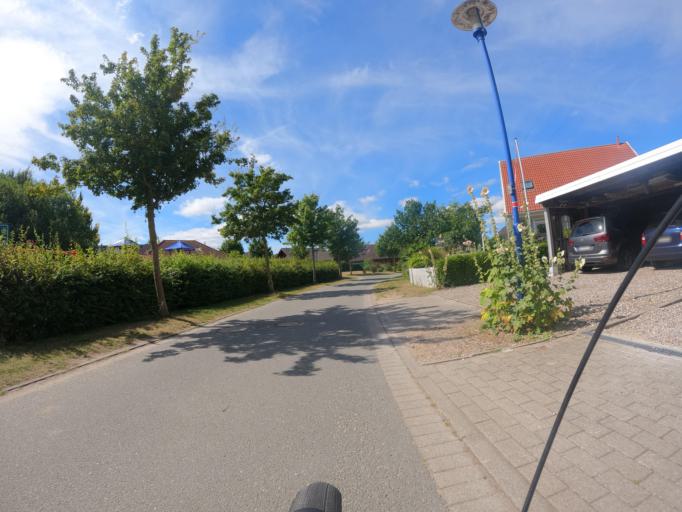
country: DE
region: Schleswig-Holstein
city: Steinbergkirche
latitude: 54.7586
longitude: 9.7599
